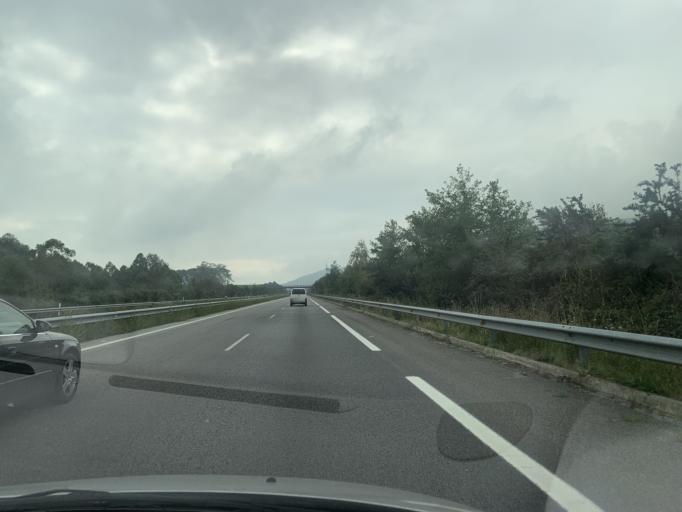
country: ES
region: Asturias
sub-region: Province of Asturias
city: Coana
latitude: 43.5429
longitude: -6.7946
